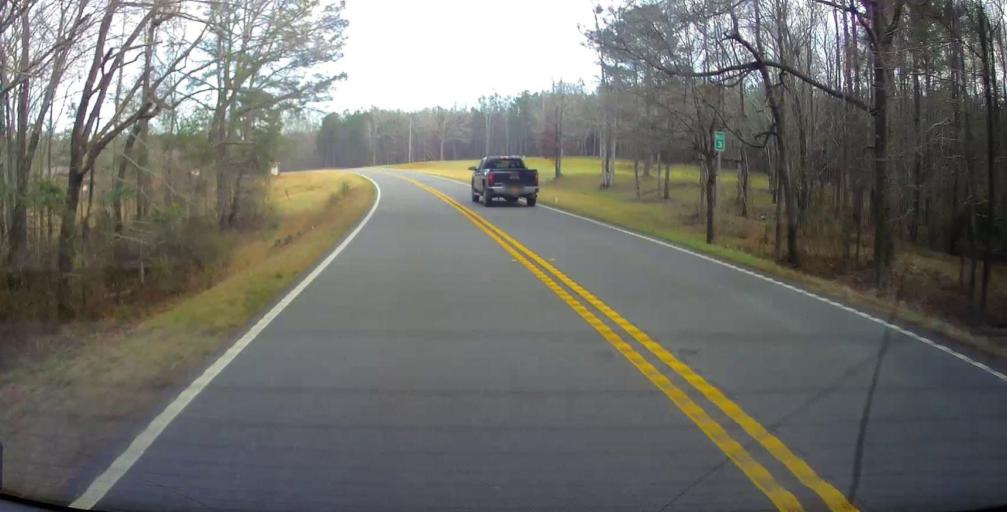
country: US
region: Georgia
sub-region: Harris County
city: Hamilton
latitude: 32.6987
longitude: -84.8106
